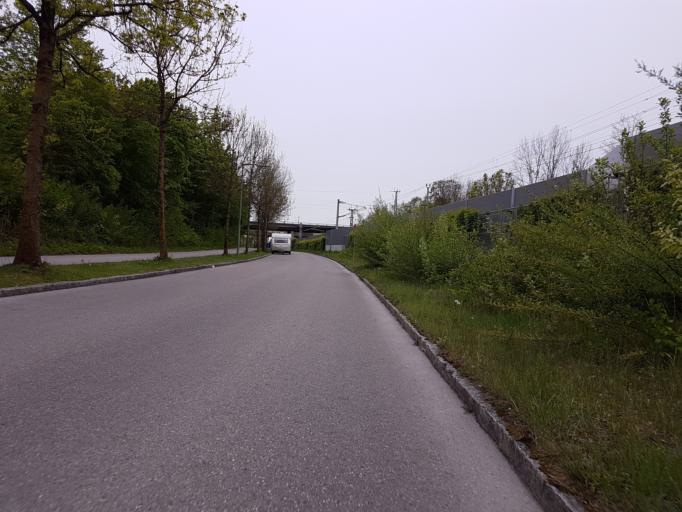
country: DE
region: Bavaria
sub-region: Upper Bavaria
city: Karlsfeld
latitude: 48.2067
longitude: 11.4618
